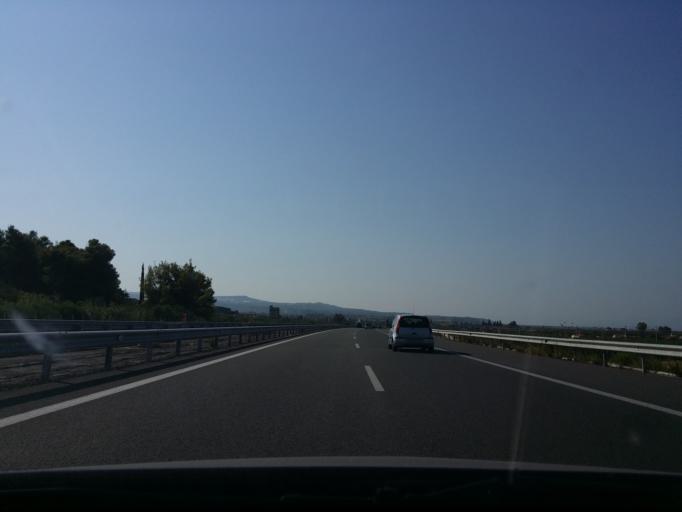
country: GR
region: Peloponnese
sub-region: Nomos Korinthias
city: Vokhaiko
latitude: 37.9421
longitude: 22.7641
